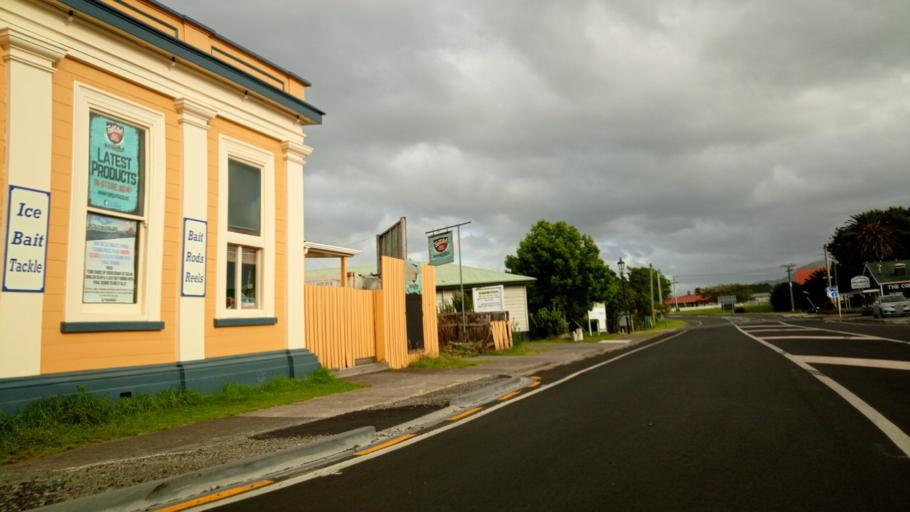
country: NZ
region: Waikato
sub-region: Thames-Coromandel District
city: Coromandel
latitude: -36.7602
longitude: 175.4973
